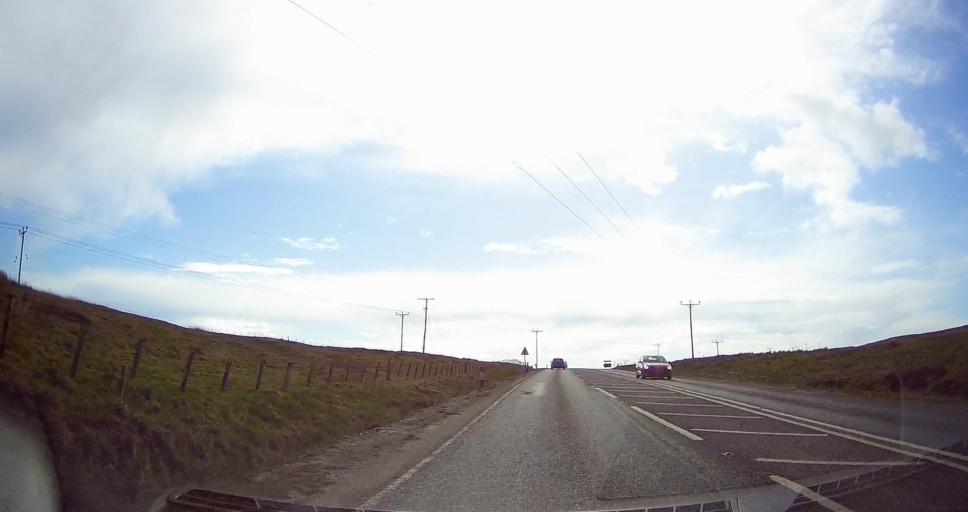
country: GB
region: Scotland
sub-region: Shetland Islands
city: Lerwick
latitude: 60.1683
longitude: -1.1922
